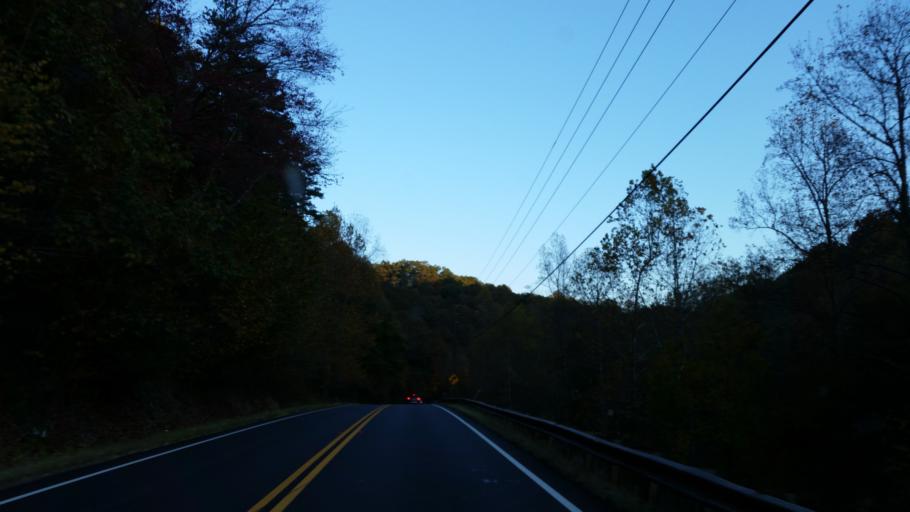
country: US
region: Georgia
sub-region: Lumpkin County
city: Dahlonega
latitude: 34.5069
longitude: -83.9722
